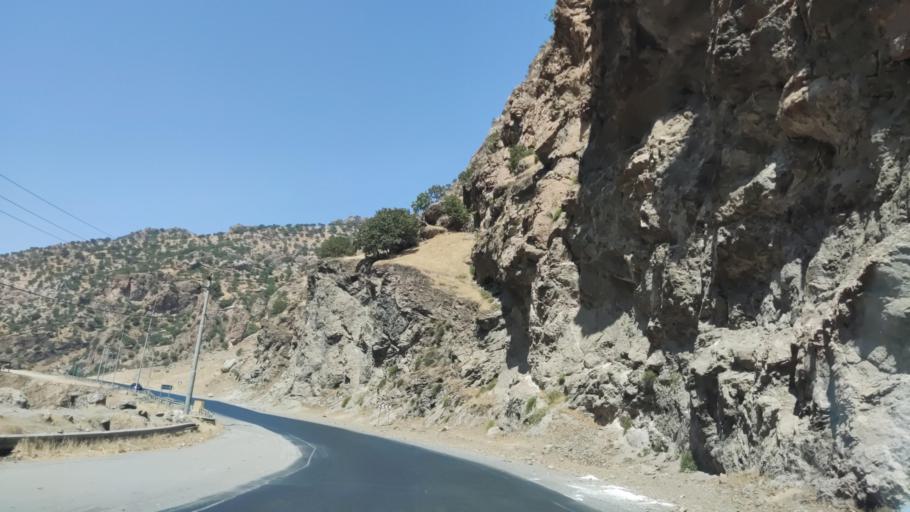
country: IQ
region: Arbil
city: Ruwandiz
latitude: 36.6313
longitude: 44.4805
